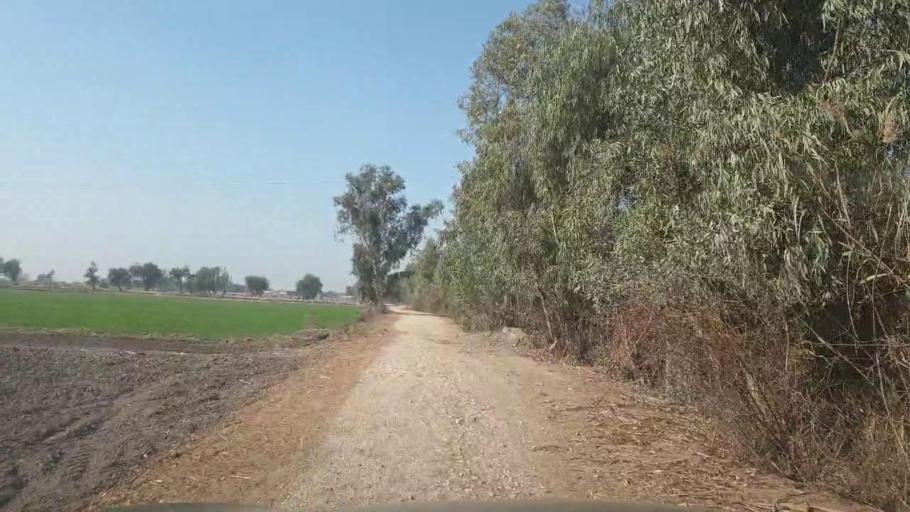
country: PK
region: Sindh
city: Mirpur Mathelo
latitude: 27.9889
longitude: 69.4700
